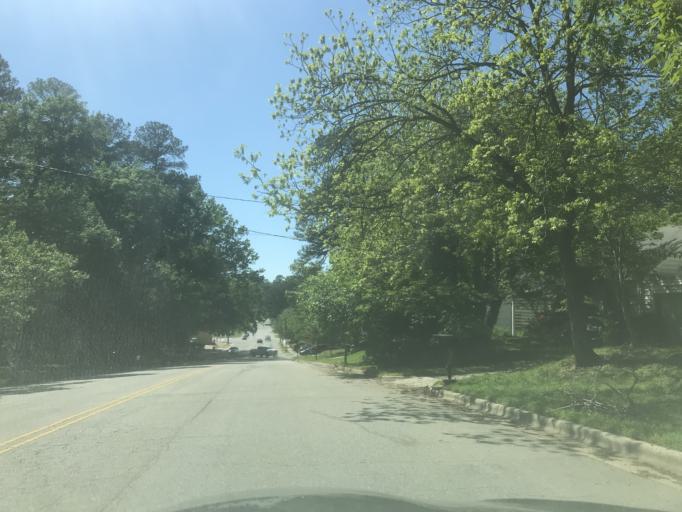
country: US
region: North Carolina
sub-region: Wake County
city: Raleigh
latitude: 35.7486
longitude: -78.6467
